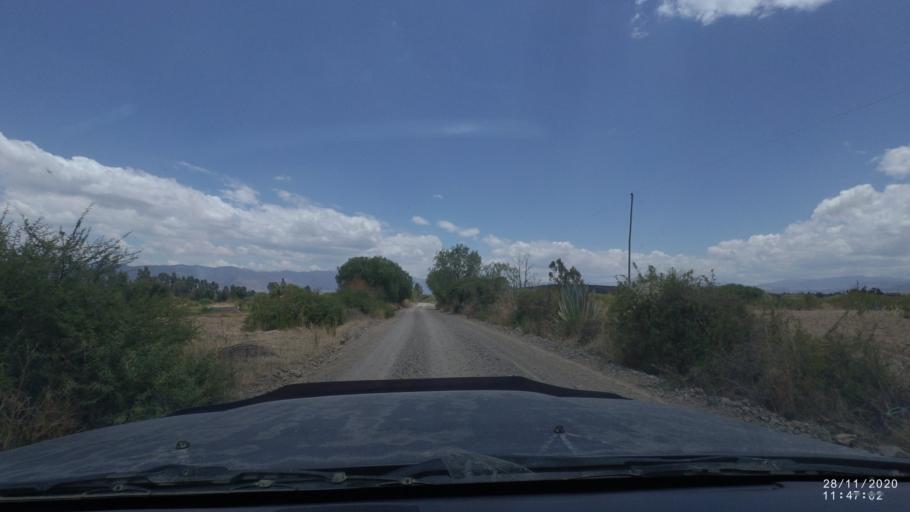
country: BO
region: Cochabamba
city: Tarata
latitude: -17.6476
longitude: -66.0392
